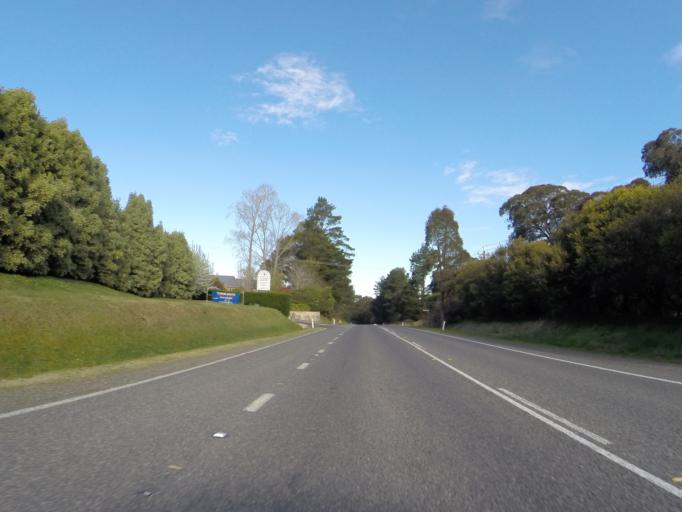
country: AU
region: New South Wales
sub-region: Wingecarribee
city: Moss Vale
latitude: -34.5629
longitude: 150.4027
